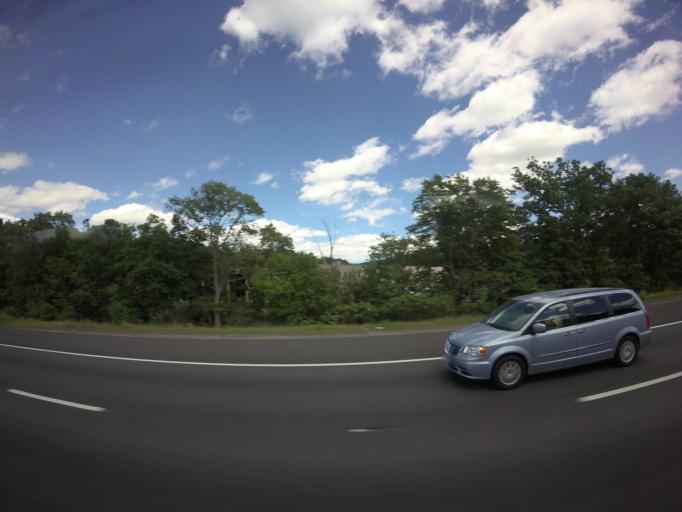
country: US
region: Massachusetts
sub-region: Middlesex County
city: Reading
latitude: 42.5319
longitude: -71.1356
